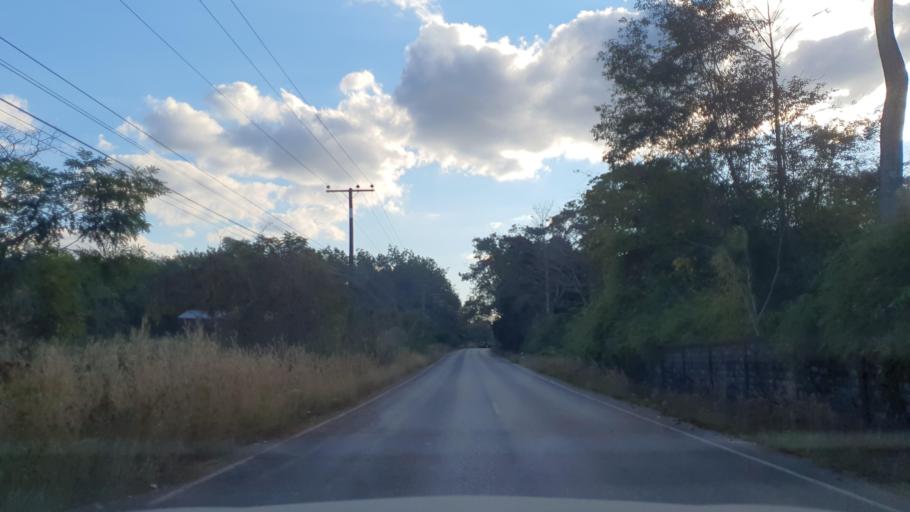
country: TH
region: Changwat Bueng Kan
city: Si Wilai
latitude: 18.1354
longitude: 103.8864
